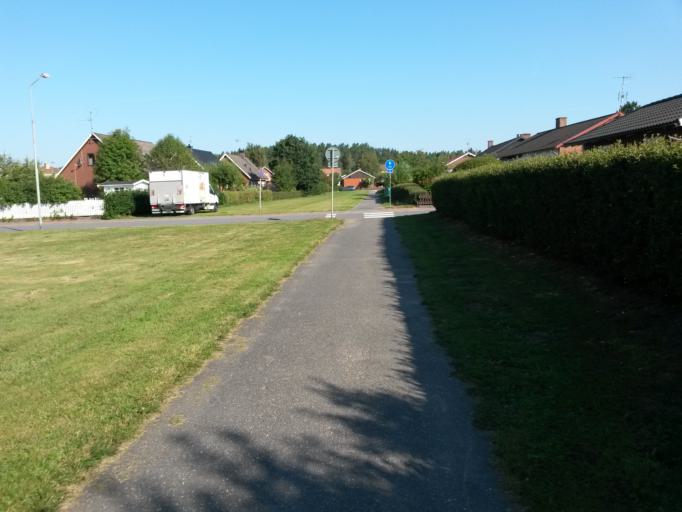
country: SE
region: Vaestra Goetaland
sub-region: Vargarda Kommun
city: Vargarda
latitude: 58.0356
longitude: 12.8140
